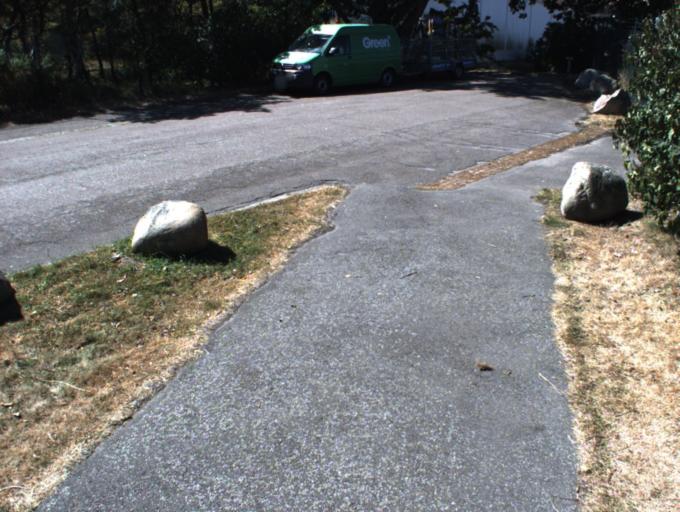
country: SE
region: Skane
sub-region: Helsingborg
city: Helsingborg
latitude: 56.0259
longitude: 12.7061
